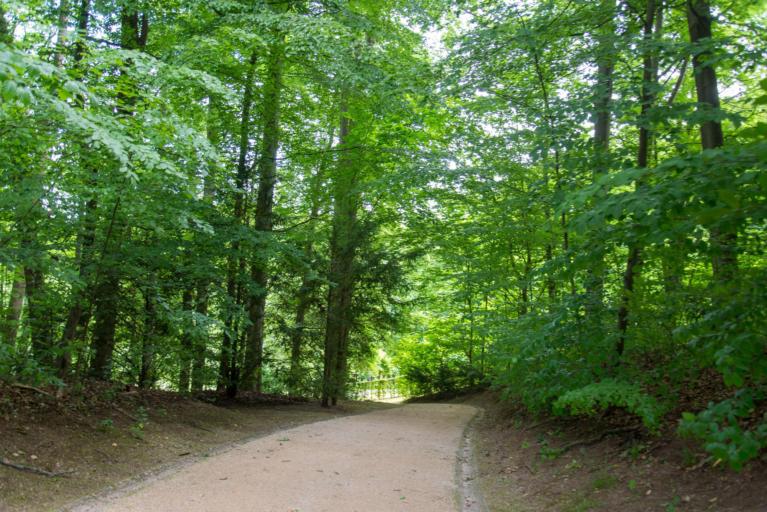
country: DE
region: Bavaria
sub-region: Upper Franconia
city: Bindlach
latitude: 49.9511
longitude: 11.6240
